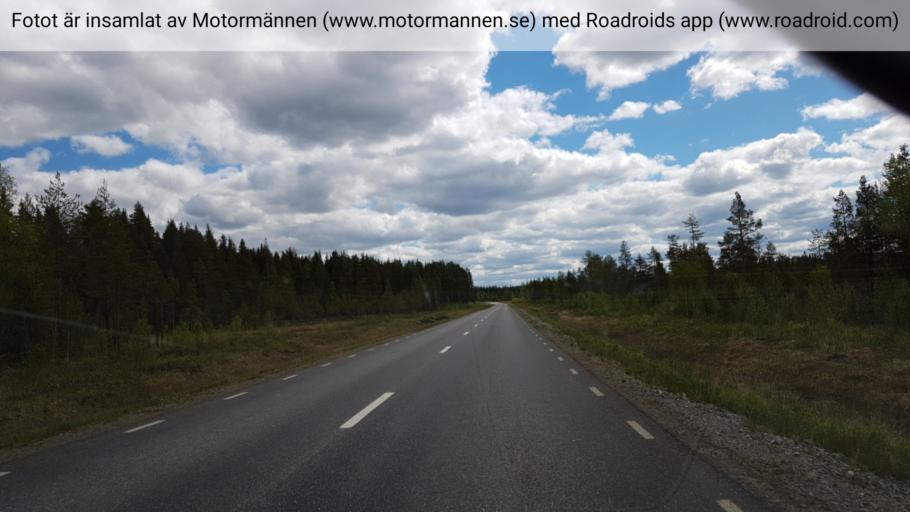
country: SE
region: Vaesterbotten
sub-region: Norsjo Kommun
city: Norsjoe
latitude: 64.8957
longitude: 19.5743
